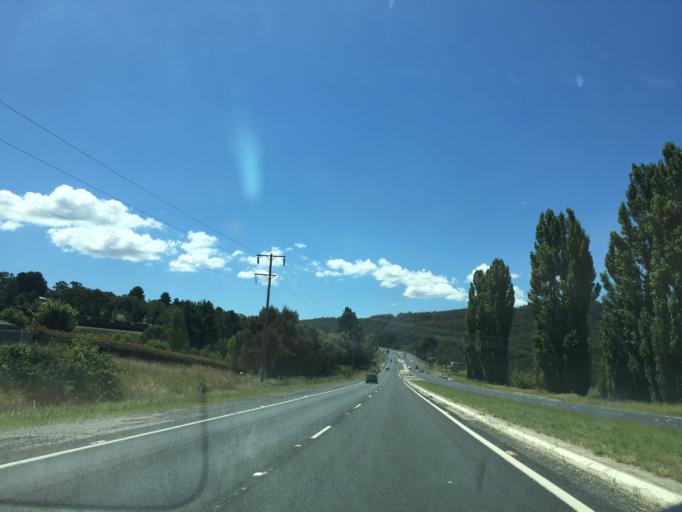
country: AU
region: New South Wales
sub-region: Lithgow
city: Lithgow
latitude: -33.4392
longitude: 150.1138
